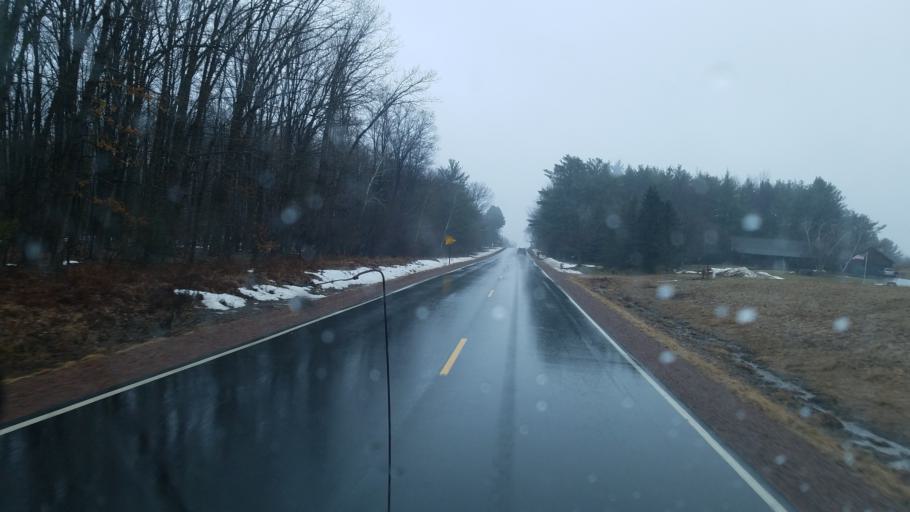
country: US
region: Wisconsin
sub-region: Wood County
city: Marshfield
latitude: 44.5456
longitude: -90.3000
